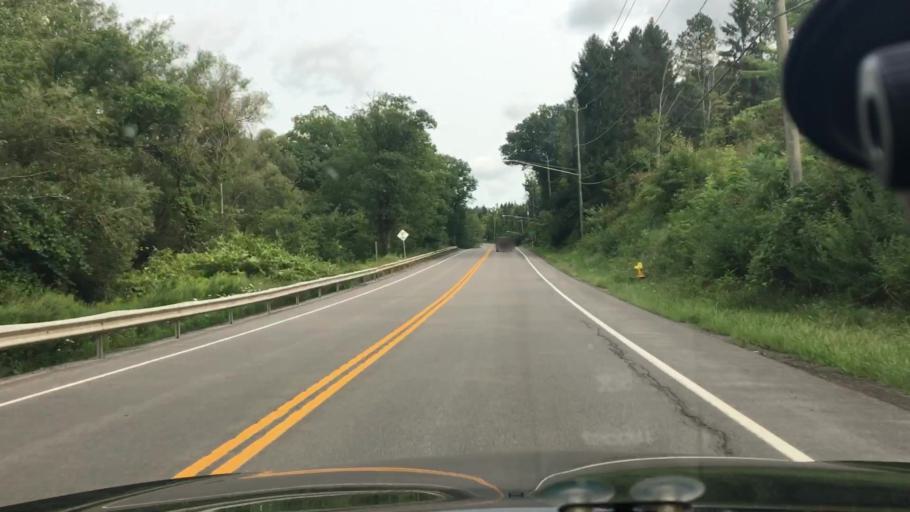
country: US
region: New York
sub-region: Erie County
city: Orchard Park
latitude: 42.7378
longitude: -78.7352
